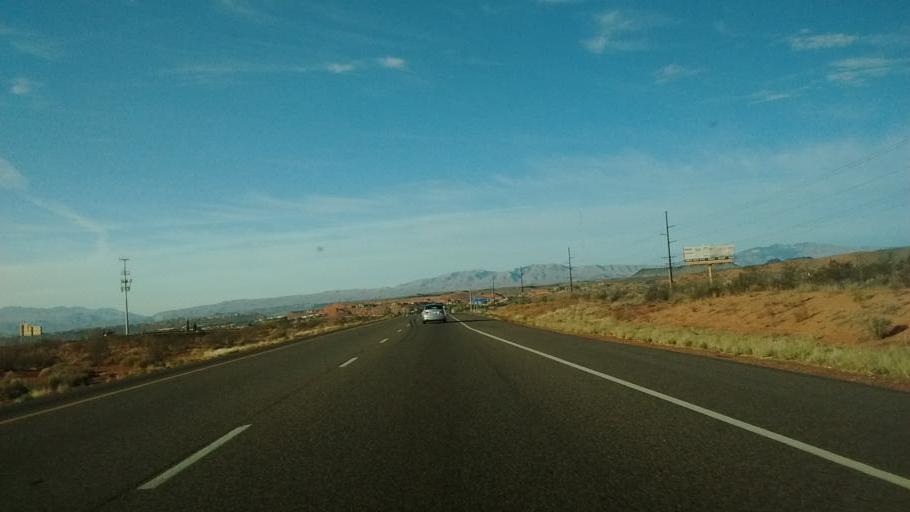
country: US
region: Utah
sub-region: Washington County
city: Washington
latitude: 37.1439
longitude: -113.4979
